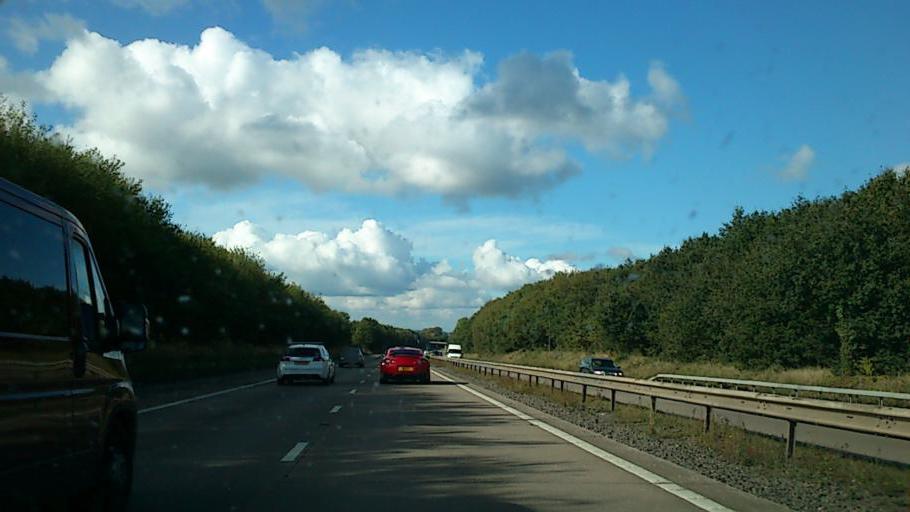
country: GB
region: England
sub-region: Shropshire
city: Albrighton
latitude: 52.6502
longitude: -2.2495
